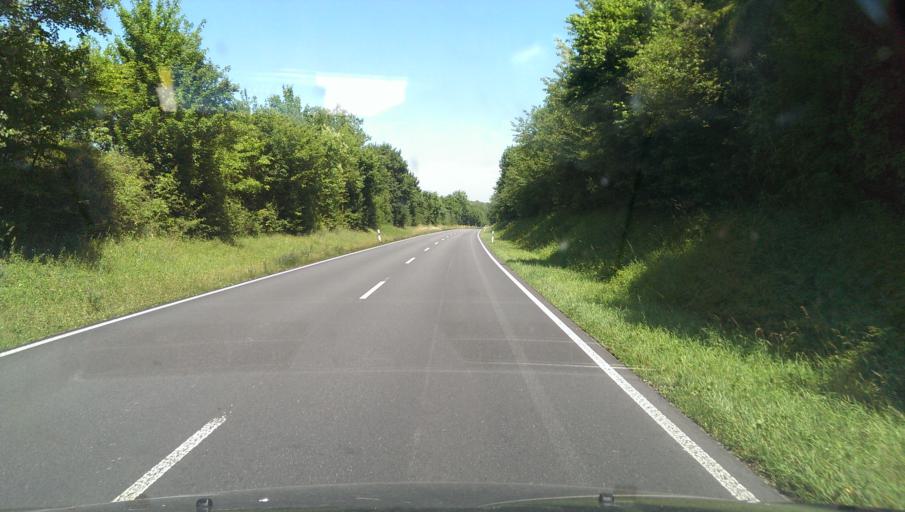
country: DE
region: Baden-Wuerttemberg
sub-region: Karlsruhe Region
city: Zaisenhausen
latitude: 49.1032
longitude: 8.8150
